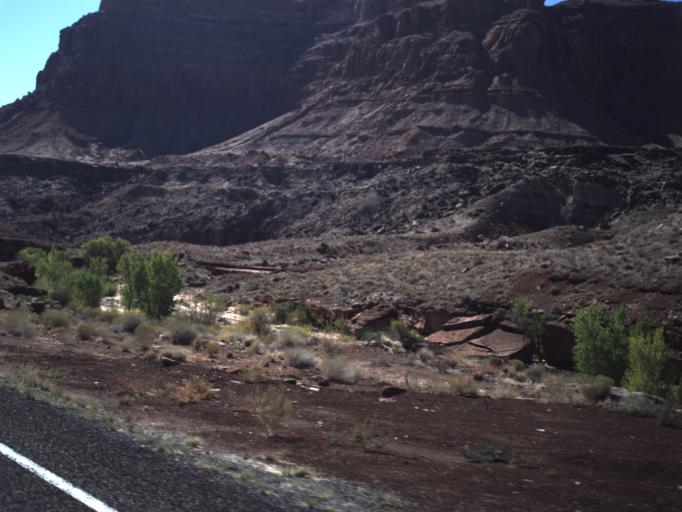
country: US
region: Utah
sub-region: San Juan County
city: Blanding
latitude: 37.8987
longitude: -110.4485
